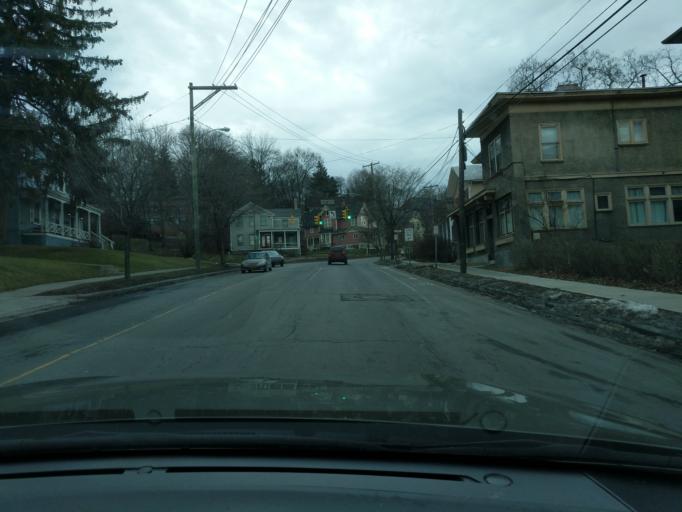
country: US
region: New York
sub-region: Tompkins County
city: Ithaca
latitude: 42.4393
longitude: -76.4905
